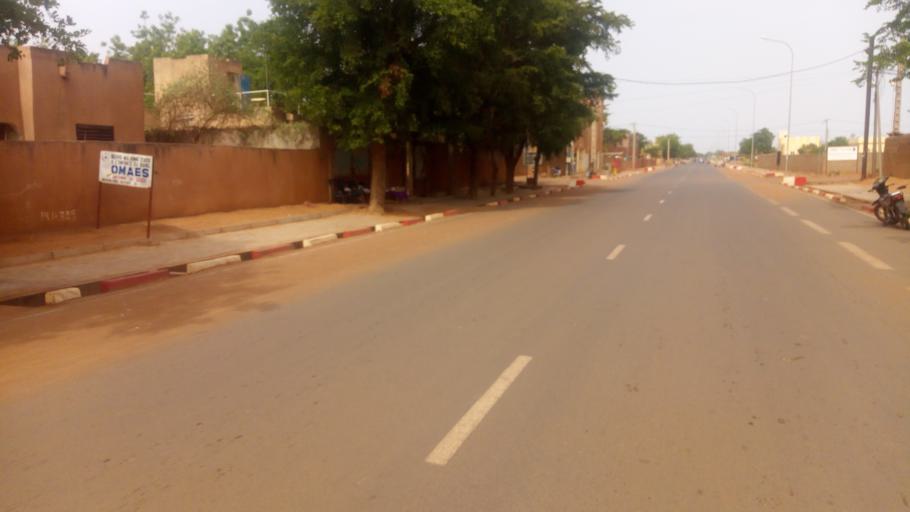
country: ML
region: Segou
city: Segou
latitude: 13.4338
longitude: -6.2705
